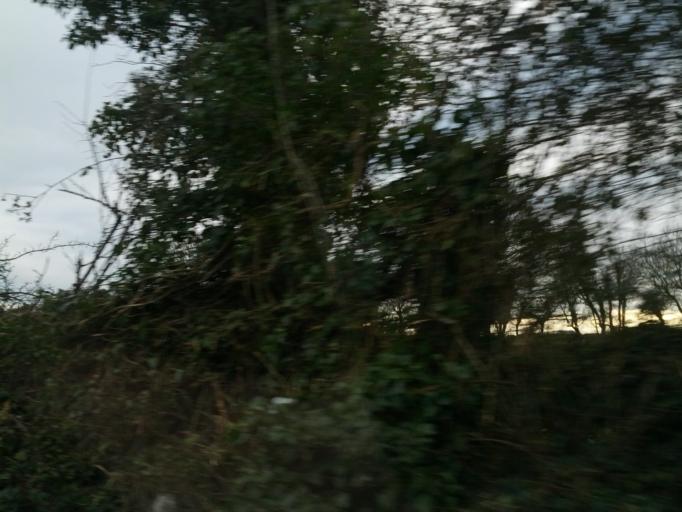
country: IE
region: Connaught
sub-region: County Galway
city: Gort
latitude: 53.1566
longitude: -8.8675
